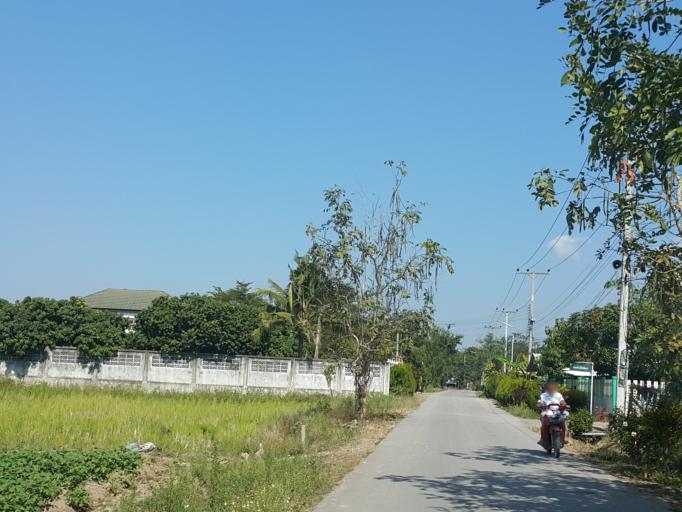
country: TH
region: Chiang Mai
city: San Sai
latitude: 18.9595
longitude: 98.9879
